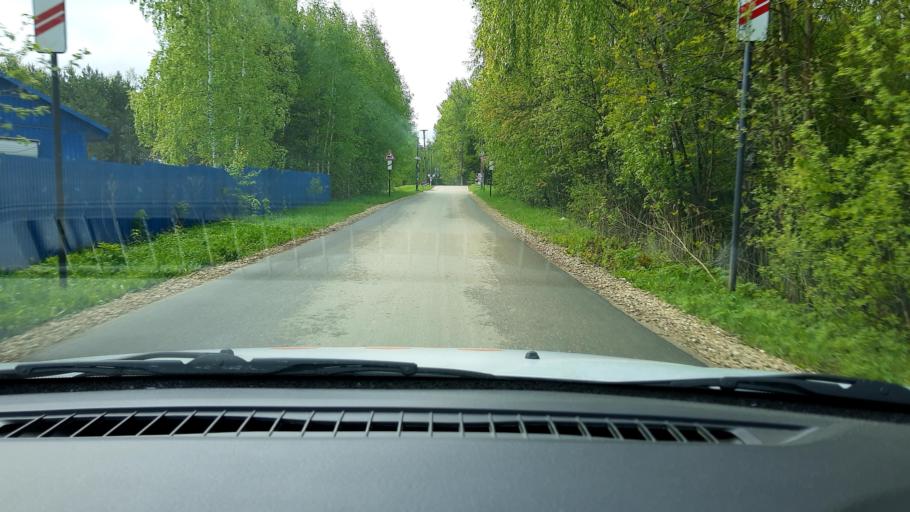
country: RU
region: Nizjnij Novgorod
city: Afonino
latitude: 56.1890
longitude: 44.0765
